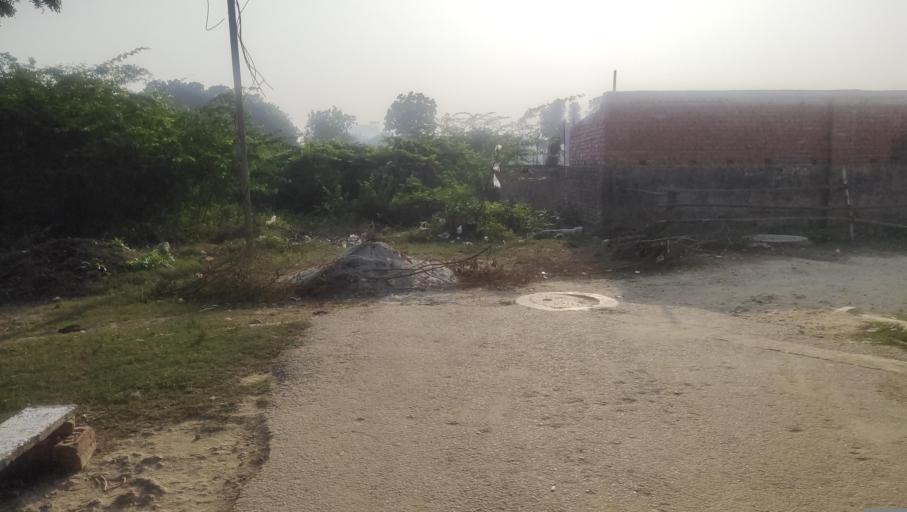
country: IN
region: Uttar Pradesh
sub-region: Lucknow District
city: Goshainganj
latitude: 26.7898
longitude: 81.0123
